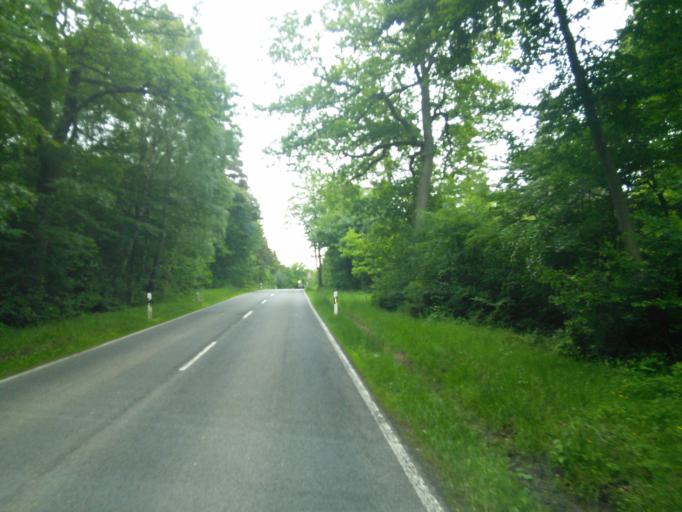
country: DE
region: Rheinland-Pfalz
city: Berg
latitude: 50.5685
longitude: 6.9110
